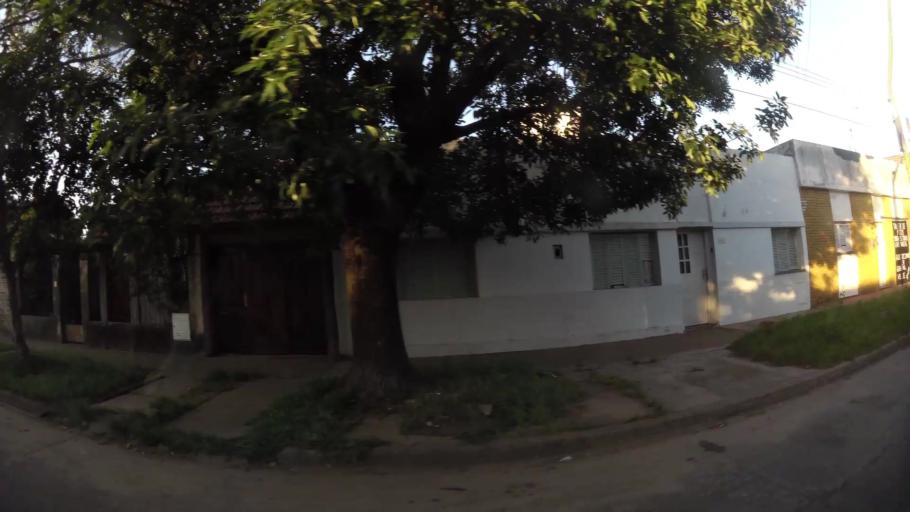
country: AR
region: Santa Fe
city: Santa Fe de la Vera Cruz
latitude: -31.6006
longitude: -60.6901
